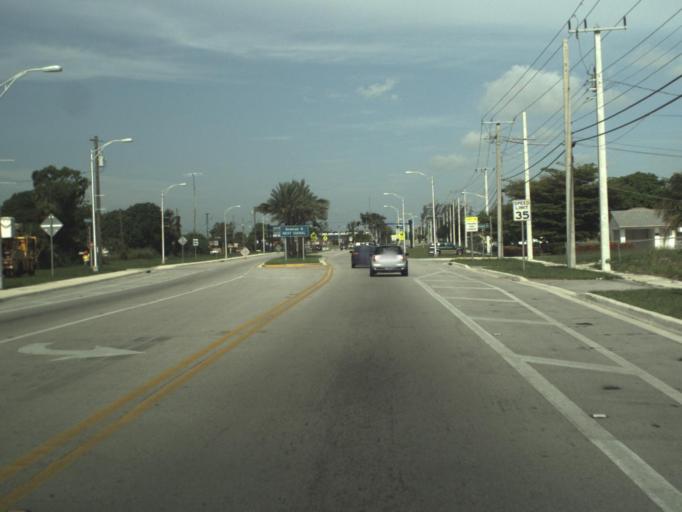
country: US
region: Florida
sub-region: Palm Beach County
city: Mangonia Park
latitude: 26.7697
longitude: -80.0720
